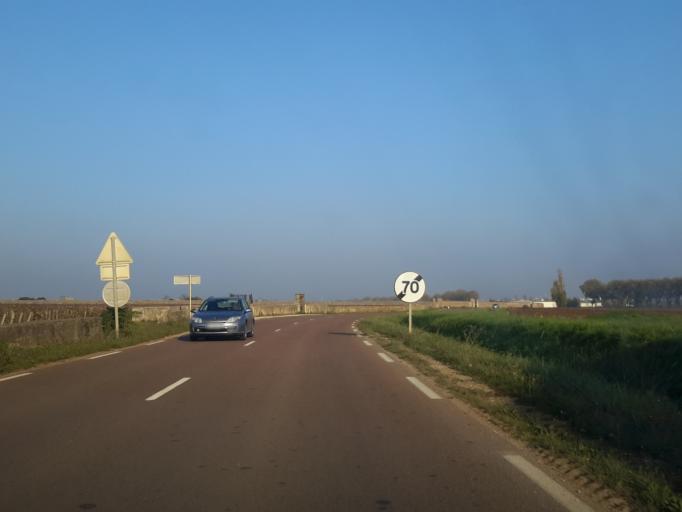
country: FR
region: Bourgogne
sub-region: Departement de la Cote-d'Or
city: Bligny-les-Beaune
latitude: 47.0112
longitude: 4.8028
